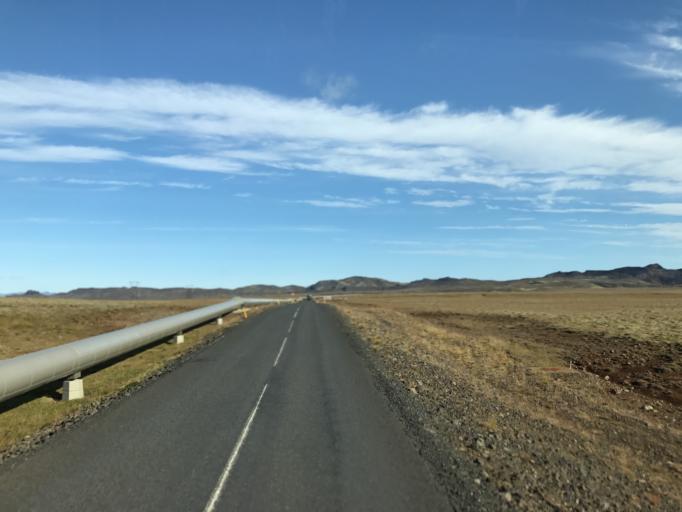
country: IS
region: South
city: Hveragerdi
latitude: 64.1220
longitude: -21.3979
